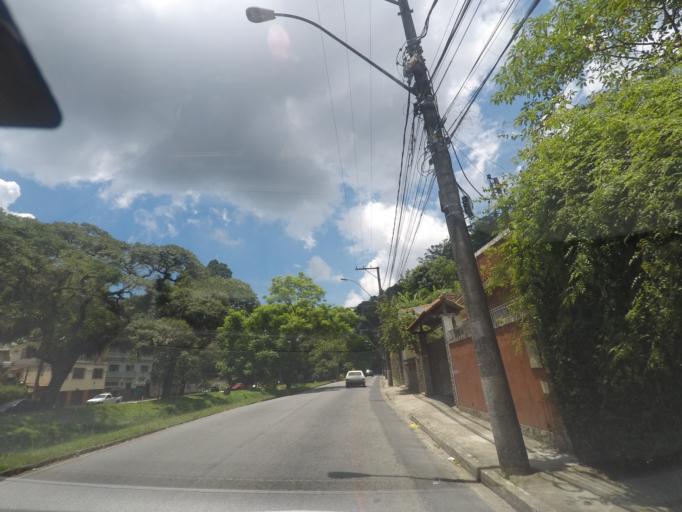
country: BR
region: Rio de Janeiro
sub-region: Petropolis
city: Petropolis
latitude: -22.4963
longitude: -43.1802
